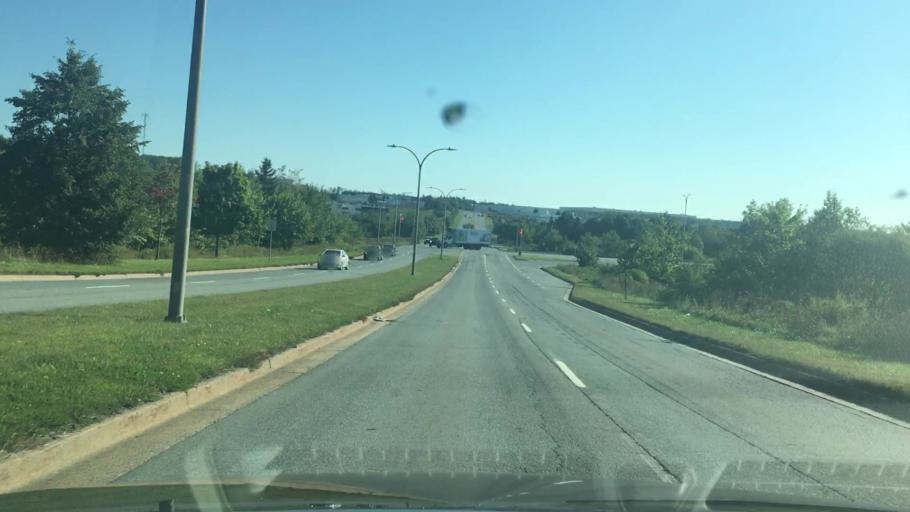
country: CA
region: Nova Scotia
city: Dartmouth
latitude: 44.7139
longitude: -63.5928
